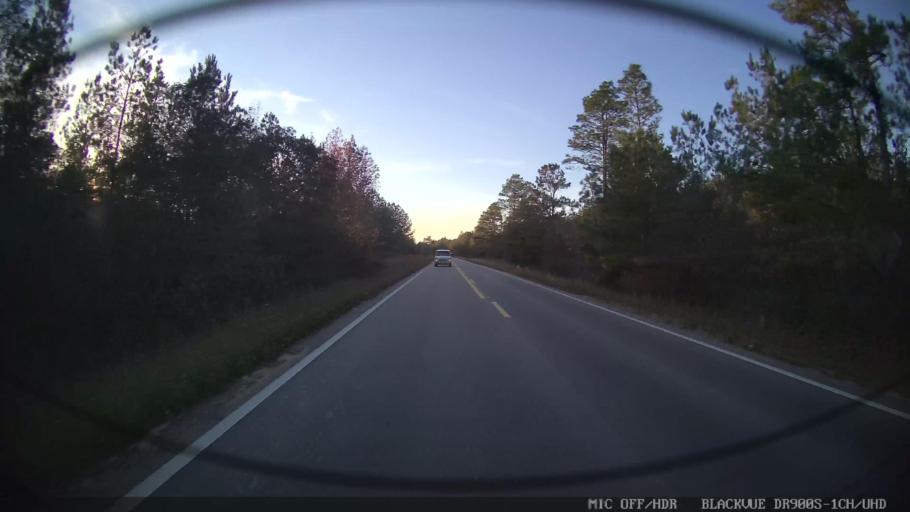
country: US
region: Mississippi
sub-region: Lamar County
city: Lumberton
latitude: 30.9997
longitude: -89.3043
